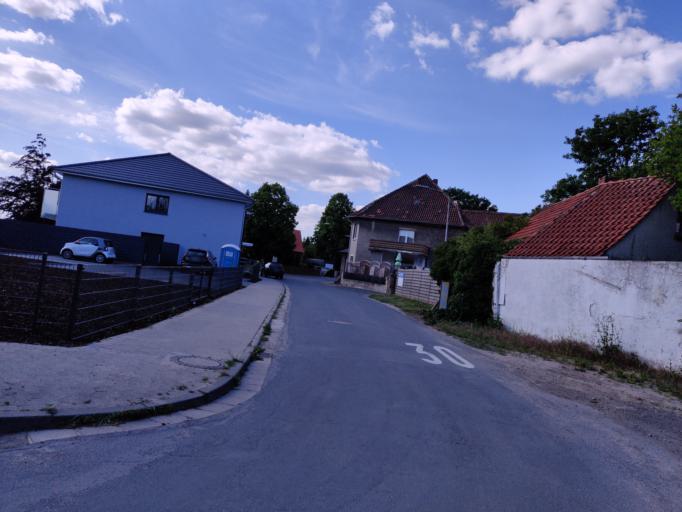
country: DE
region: Lower Saxony
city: Wunstorf
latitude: 52.4316
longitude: 9.4760
